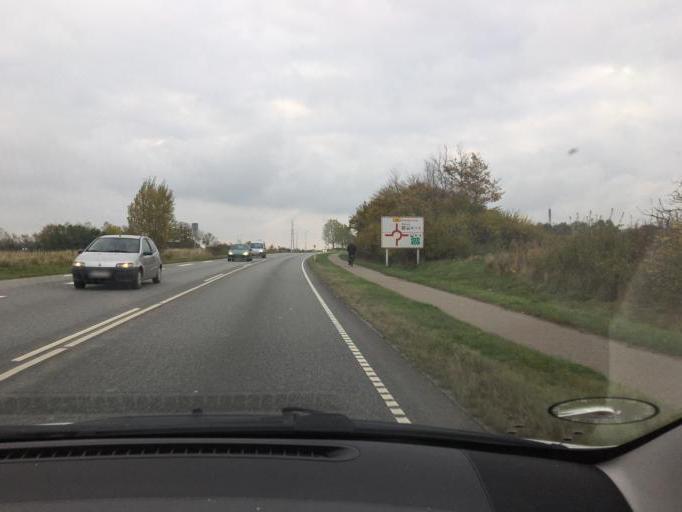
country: DK
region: South Denmark
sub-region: Fredericia Kommune
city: Fredericia
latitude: 55.6029
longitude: 9.7583
